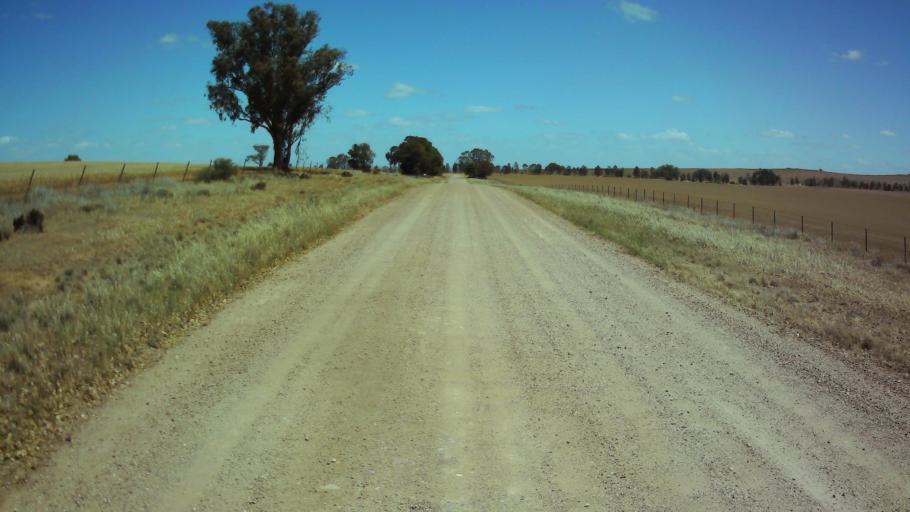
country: AU
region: New South Wales
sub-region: Weddin
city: Grenfell
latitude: -33.9502
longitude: 148.3286
